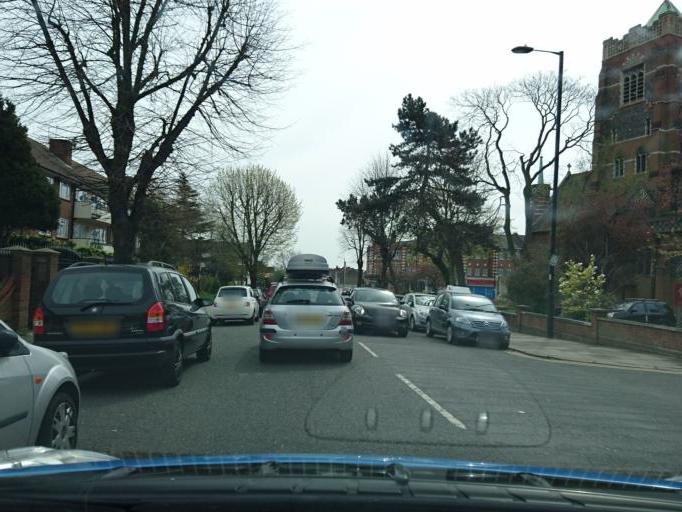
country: GB
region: England
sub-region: Greater London
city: Wood Green
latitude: 51.6242
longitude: -0.1049
